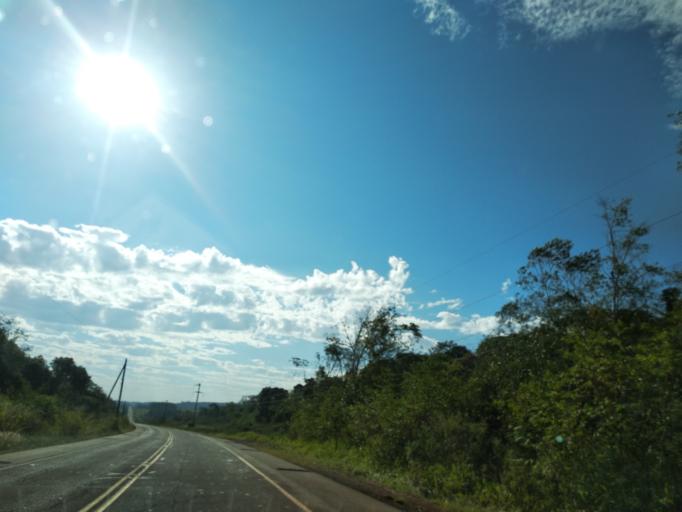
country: AR
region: Misiones
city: Aristobulo del Valle
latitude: -27.0897
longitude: -54.9776
